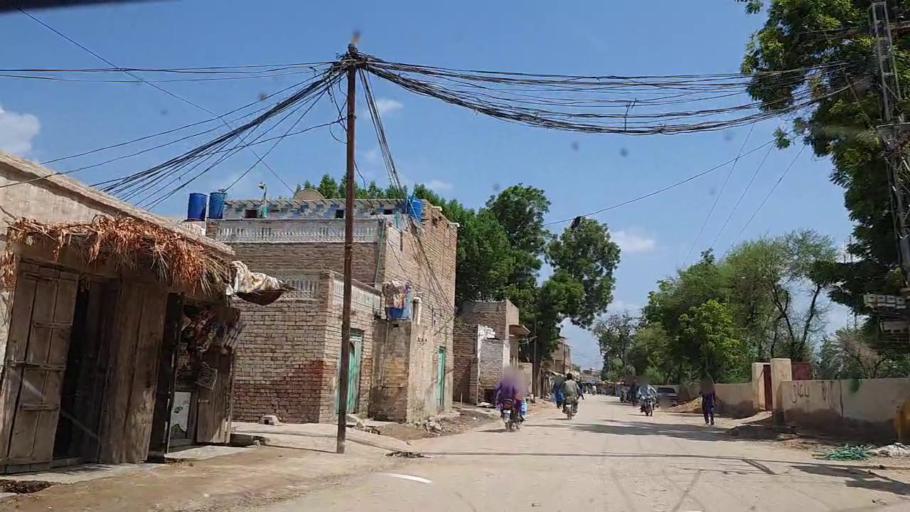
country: PK
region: Sindh
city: Tharu Shah
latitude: 26.9451
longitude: 68.1132
